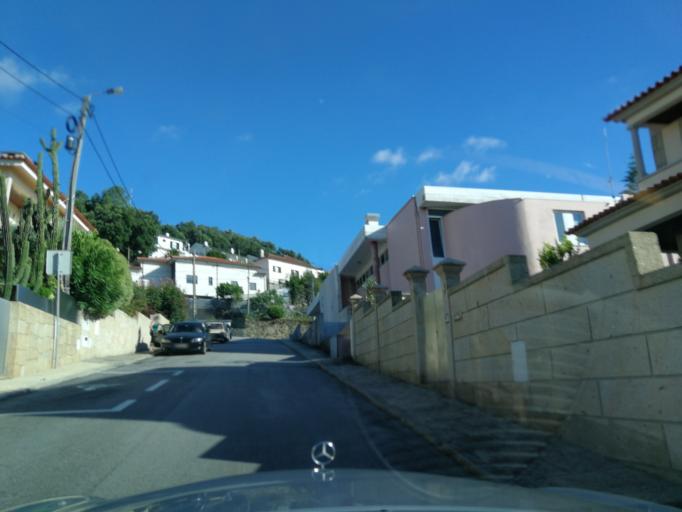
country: PT
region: Braga
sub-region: Braga
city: Braga
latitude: 41.5517
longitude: -8.3877
